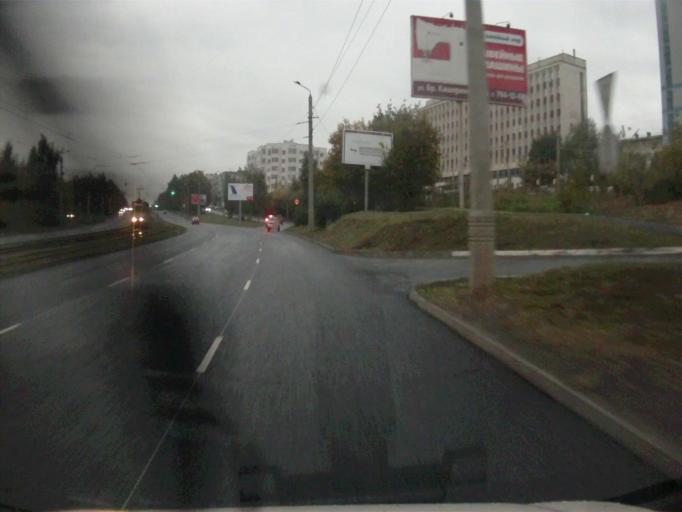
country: RU
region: Chelyabinsk
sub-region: Gorod Chelyabinsk
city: Chelyabinsk
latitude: 55.1889
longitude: 61.3584
